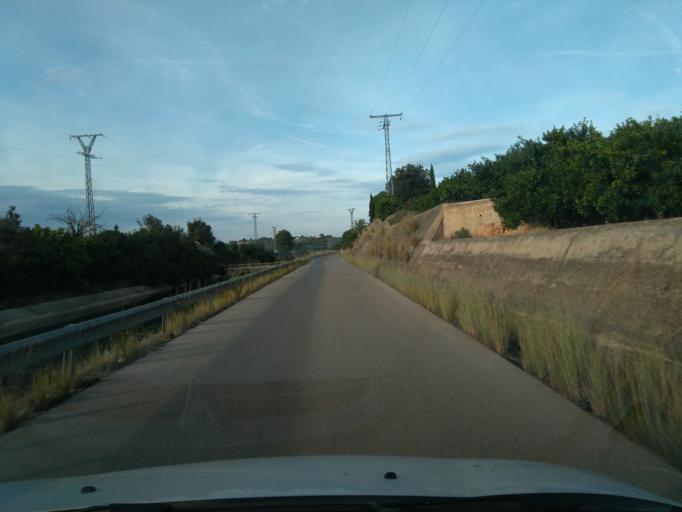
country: ES
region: Valencia
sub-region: Provincia de Valencia
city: Benimodo
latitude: 39.1942
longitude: -0.5672
